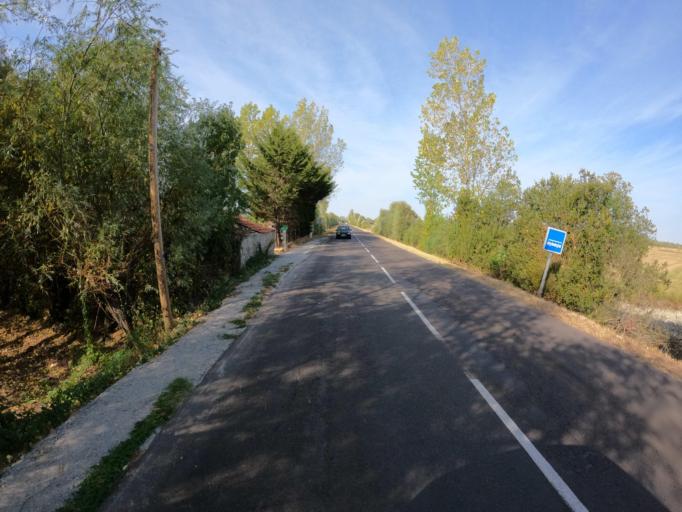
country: FR
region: Pays de la Loire
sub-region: Departement de la Vendee
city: Le Perrier
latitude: 46.8044
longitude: -1.9521
